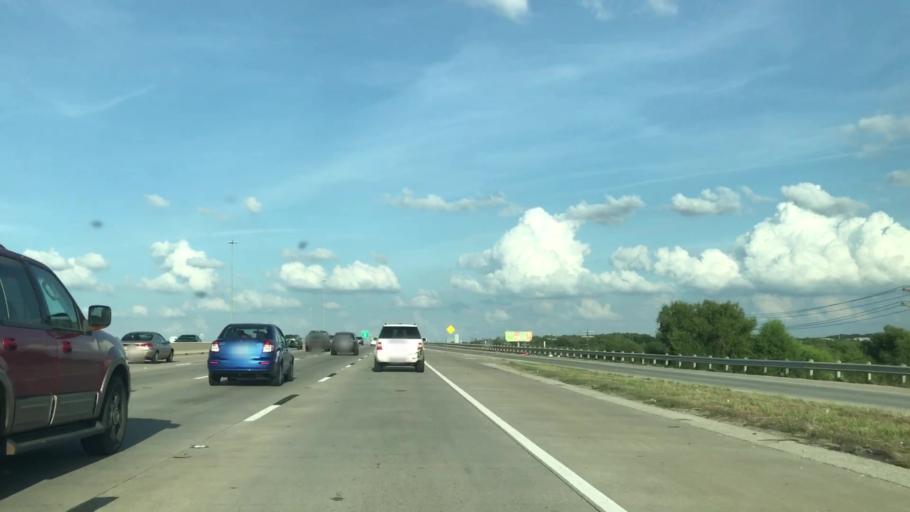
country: US
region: Texas
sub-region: Dallas County
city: Irving
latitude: 32.7632
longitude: -96.9412
